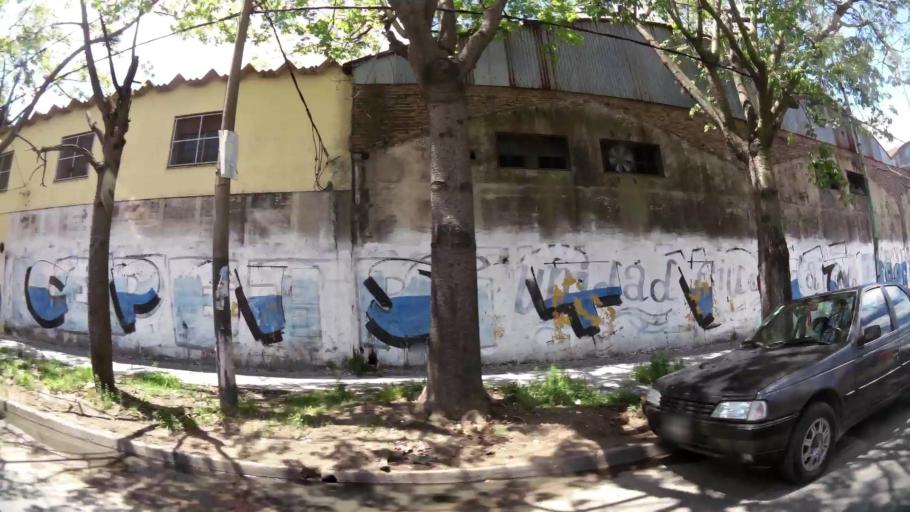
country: AR
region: Buenos Aires
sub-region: Partido de Lanus
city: Lanus
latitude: -34.7282
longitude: -58.4167
